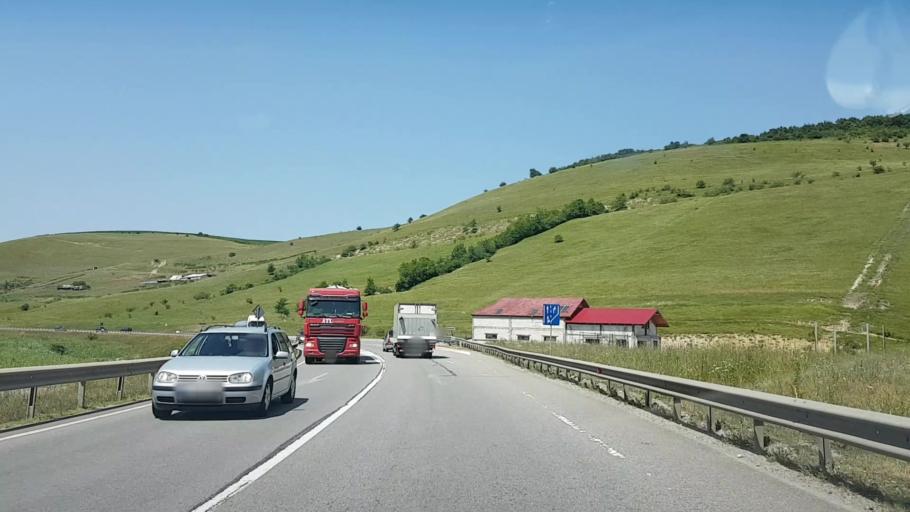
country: RO
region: Cluj
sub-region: Comuna Apahida
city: Dezmir
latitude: 46.7445
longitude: 23.7122
